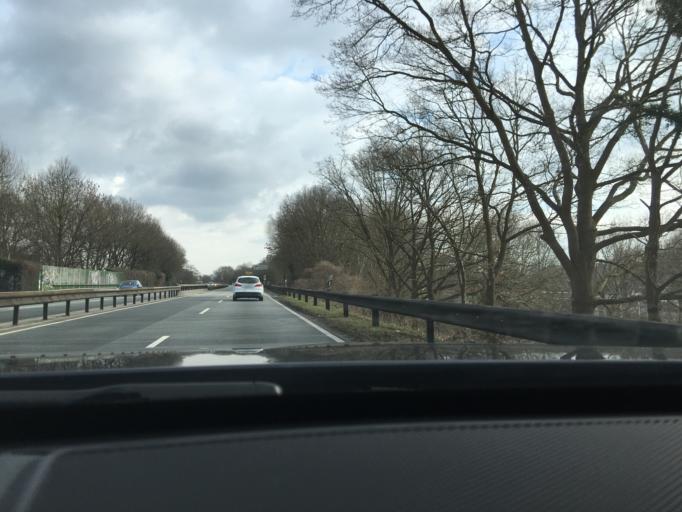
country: DE
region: Lower Saxony
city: Stuhr
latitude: 53.0535
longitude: 8.7339
